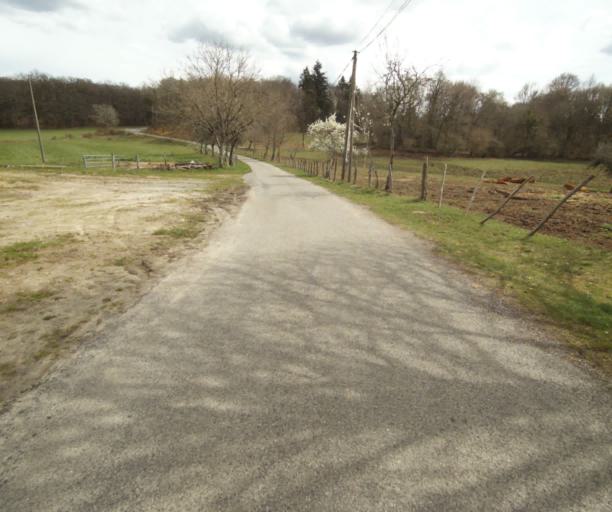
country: FR
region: Limousin
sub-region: Departement de la Correze
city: Argentat
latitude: 45.2237
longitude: 1.9186
